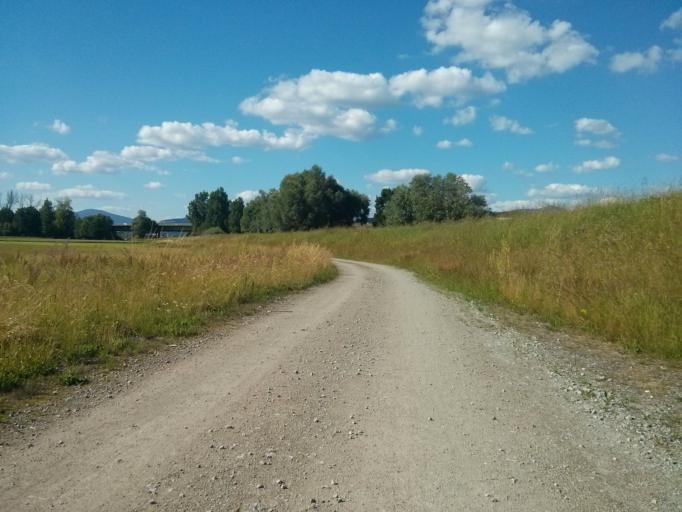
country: DE
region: Bavaria
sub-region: Lower Bavaria
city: Deggendorf
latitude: 48.8076
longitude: 12.9662
